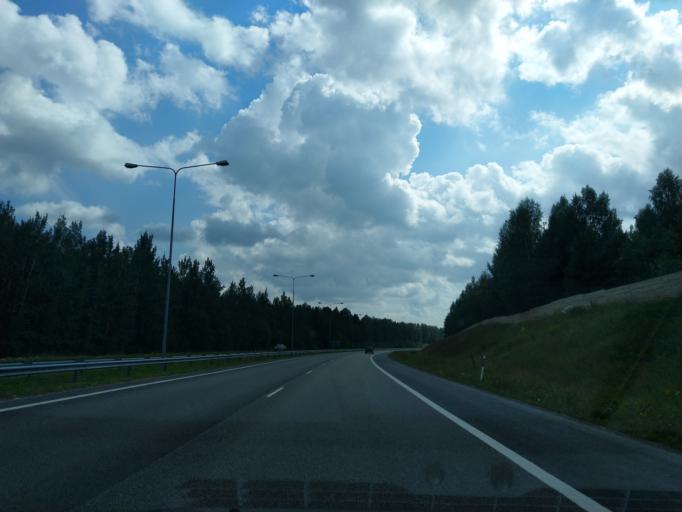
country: FI
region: South Karelia
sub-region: Imatra
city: Ruokolahti
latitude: 61.2134
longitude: 28.8481
